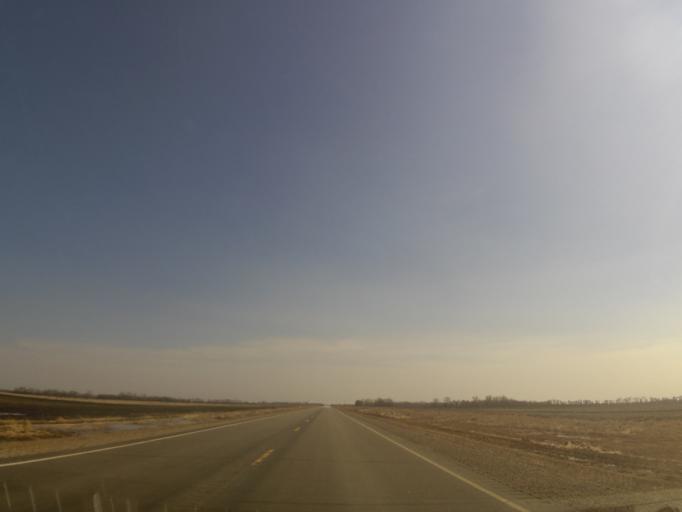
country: US
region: North Dakota
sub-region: Grand Forks County
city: Grand Forks Air Force Base
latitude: 48.1294
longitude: -97.2420
